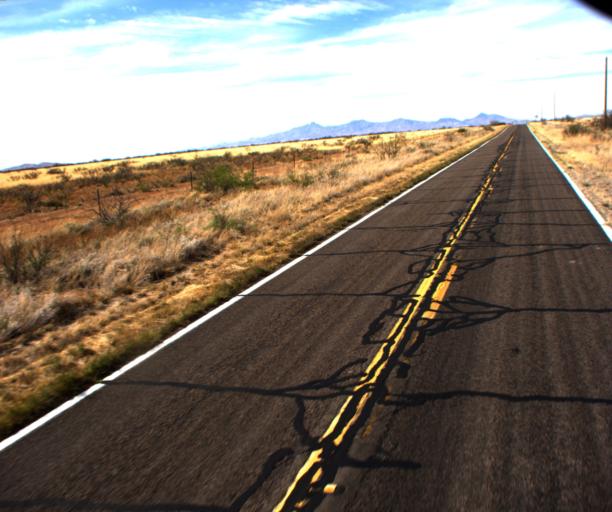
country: US
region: Arizona
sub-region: Cochise County
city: Willcox
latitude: 31.9205
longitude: -109.4914
